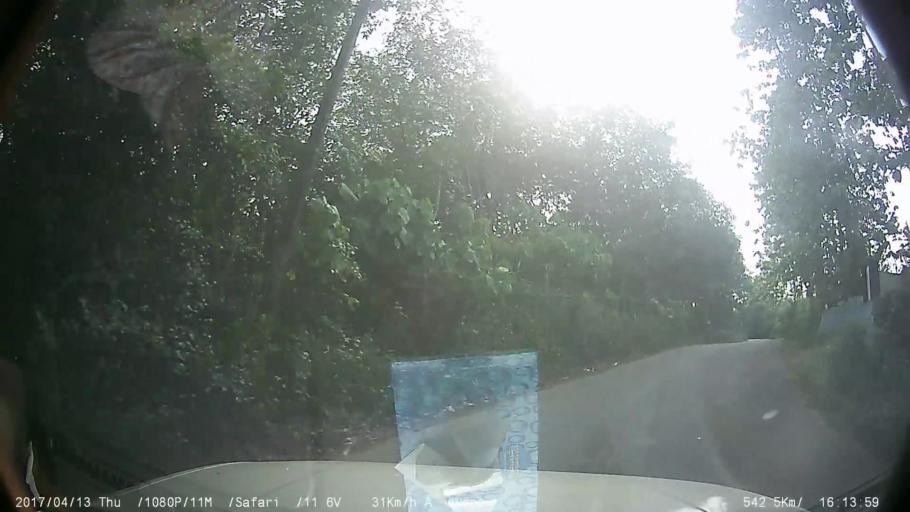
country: IN
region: Kerala
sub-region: Ernakulam
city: Piravam
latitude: 9.8226
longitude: 76.5089
